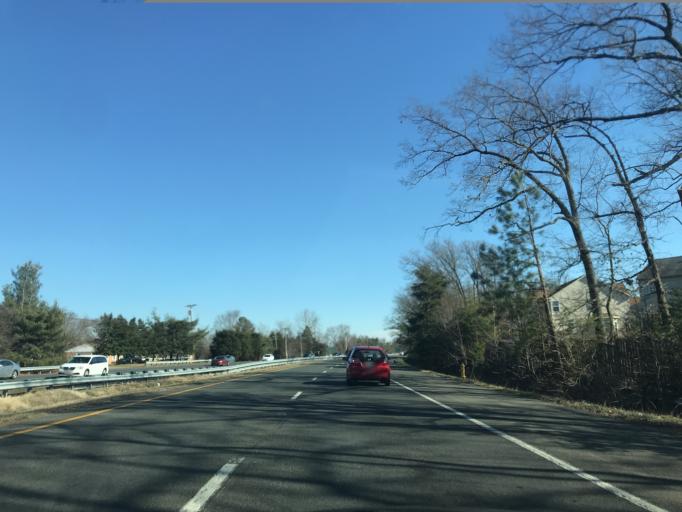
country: US
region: Maryland
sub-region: Charles County
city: Waldorf
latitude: 38.6490
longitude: -76.9432
